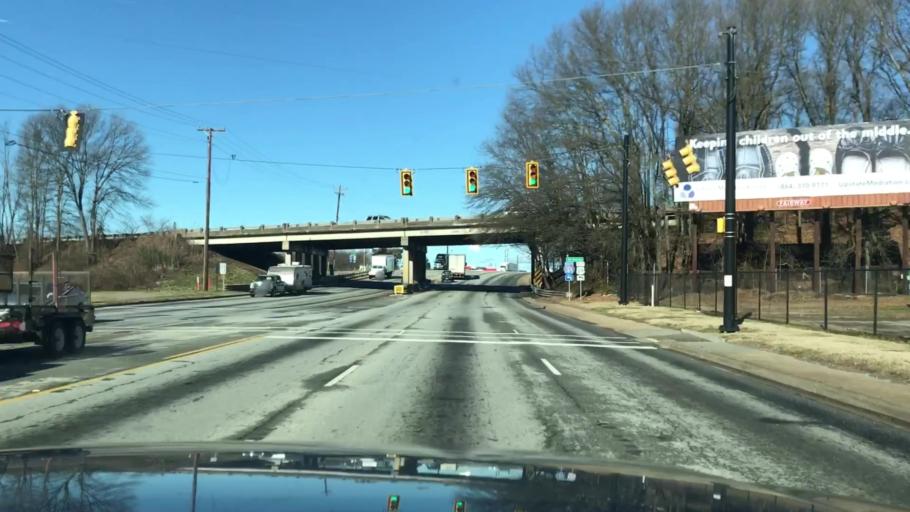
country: US
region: South Carolina
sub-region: Greenville County
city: Gantt
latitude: 34.8013
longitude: -82.4269
